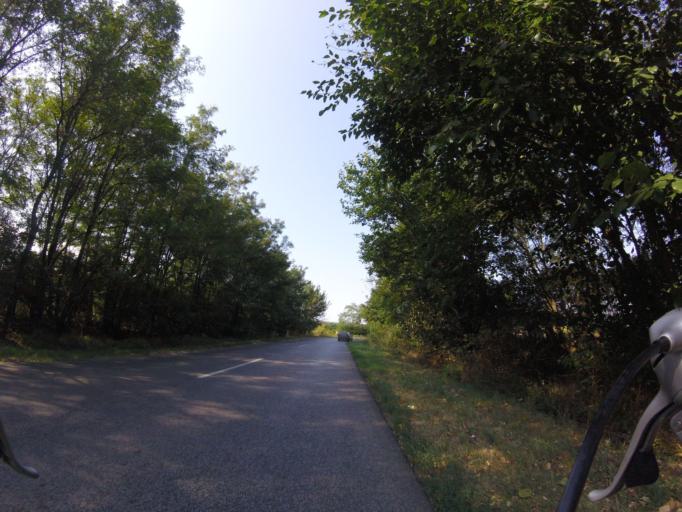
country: HU
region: Szabolcs-Szatmar-Bereg
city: Kotaj
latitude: 48.0433
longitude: 21.7394
